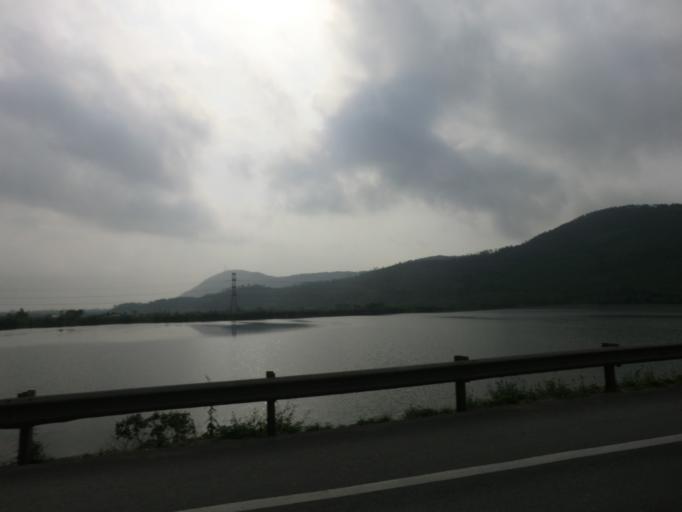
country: VN
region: Ha Tinh
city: Ky Anh
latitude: 17.9664
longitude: 106.4698
